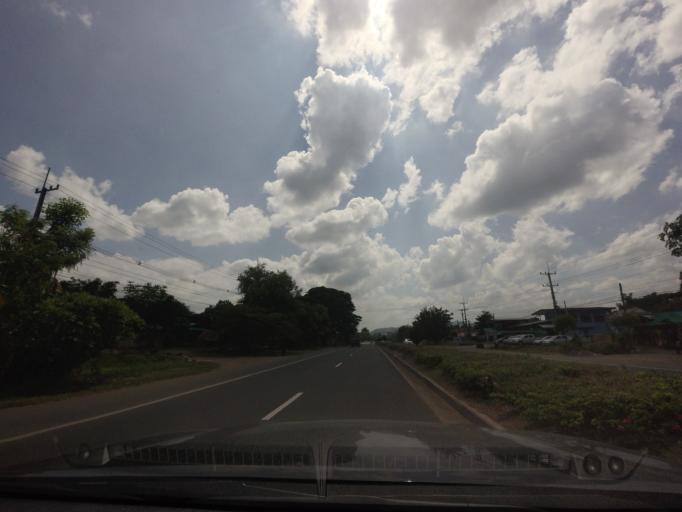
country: TH
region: Phetchabun
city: Phetchabun
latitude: 16.2736
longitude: 101.0585
